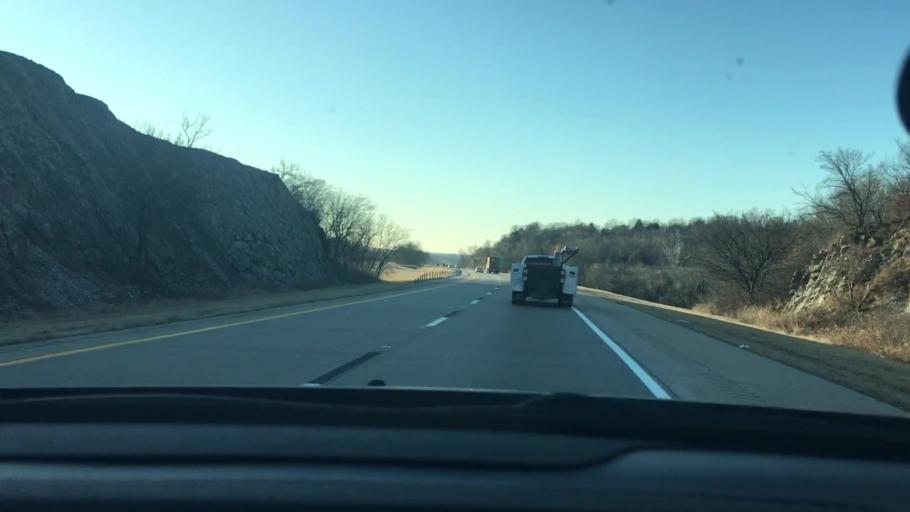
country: US
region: Oklahoma
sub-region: Murray County
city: Davis
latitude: 34.3561
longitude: -97.1492
